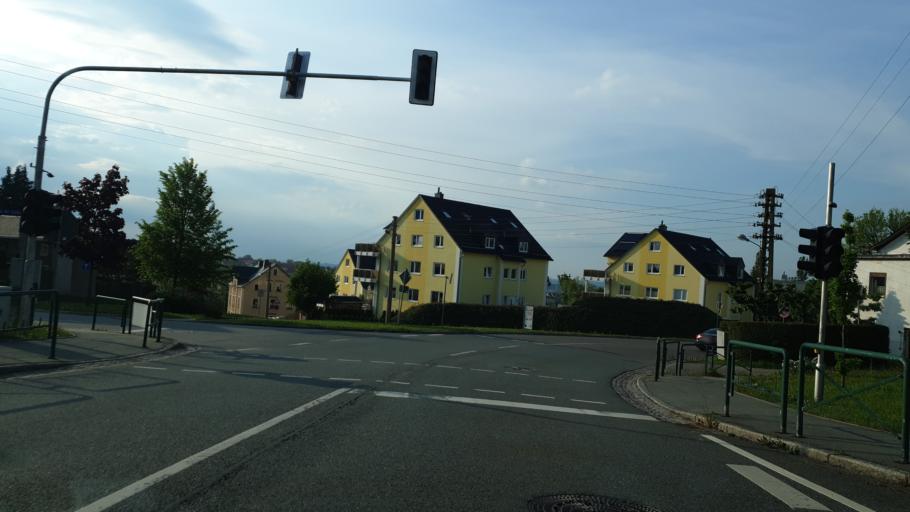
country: DE
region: Saxony
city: Stollberg
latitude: 50.7042
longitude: 12.7864
